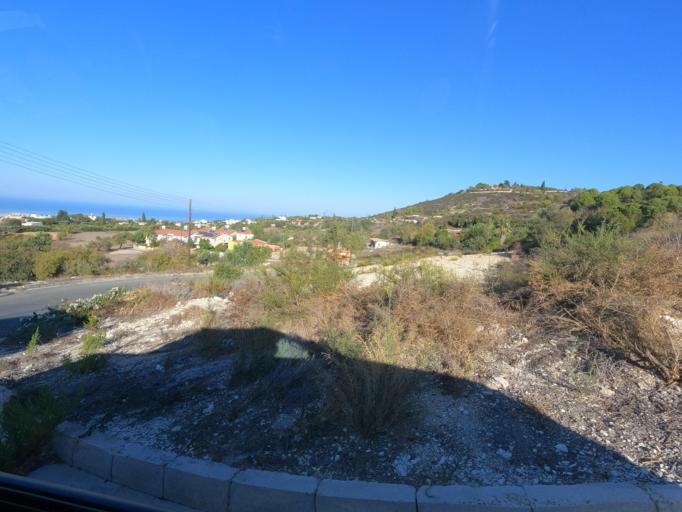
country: CY
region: Pafos
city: Mesogi
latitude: 34.7986
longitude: 32.4872
